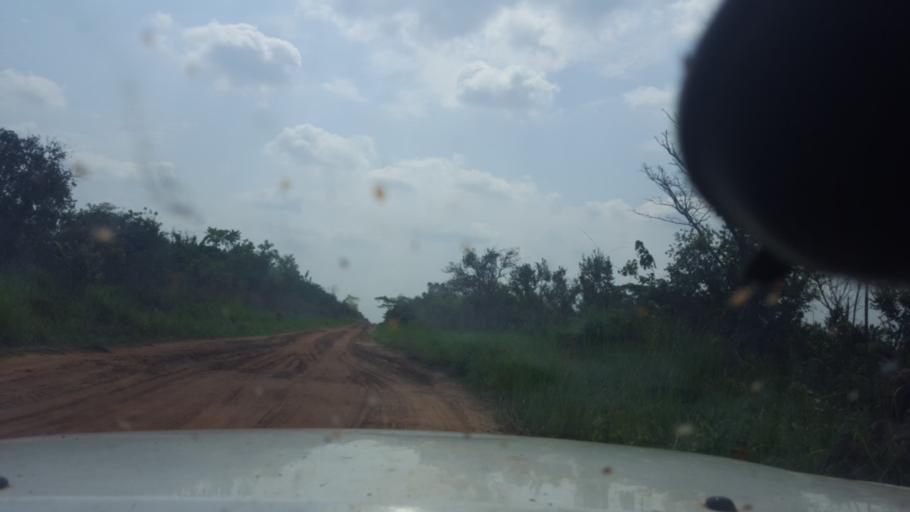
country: CD
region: Bandundu
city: Bandundu
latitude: -3.7620
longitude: 17.1439
